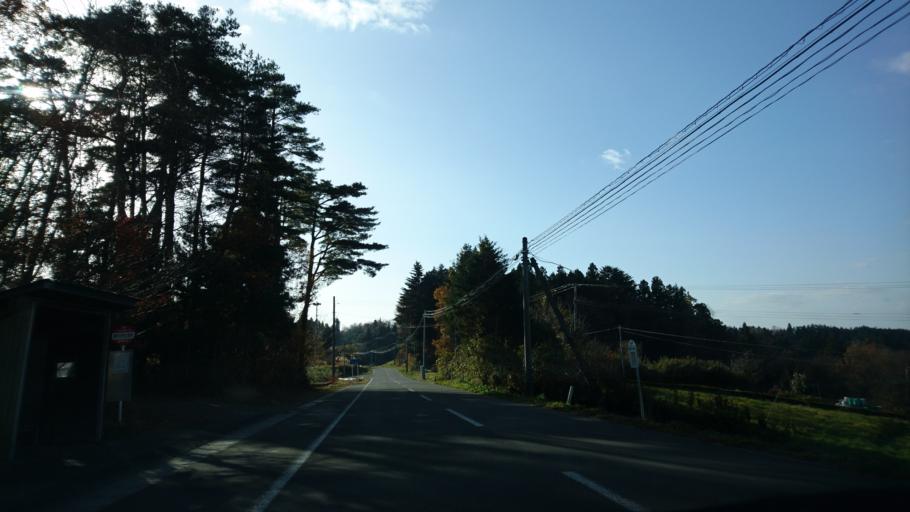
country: JP
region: Iwate
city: Ichinoseki
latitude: 38.8794
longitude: 141.2914
